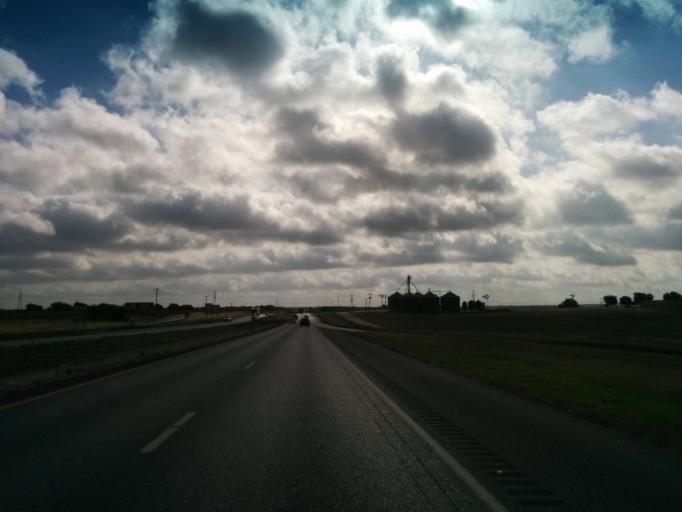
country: US
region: Texas
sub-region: Guadalupe County
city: McQueeney
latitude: 29.5408
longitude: -98.0710
